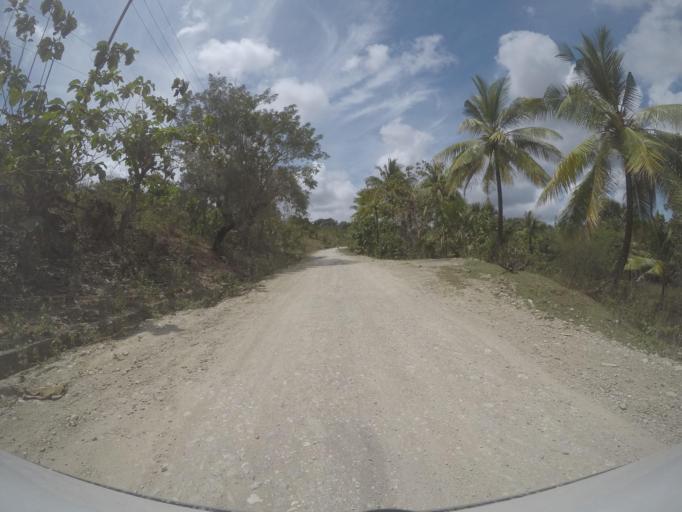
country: TL
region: Viqueque
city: Viqueque
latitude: -8.8832
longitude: 126.3791
